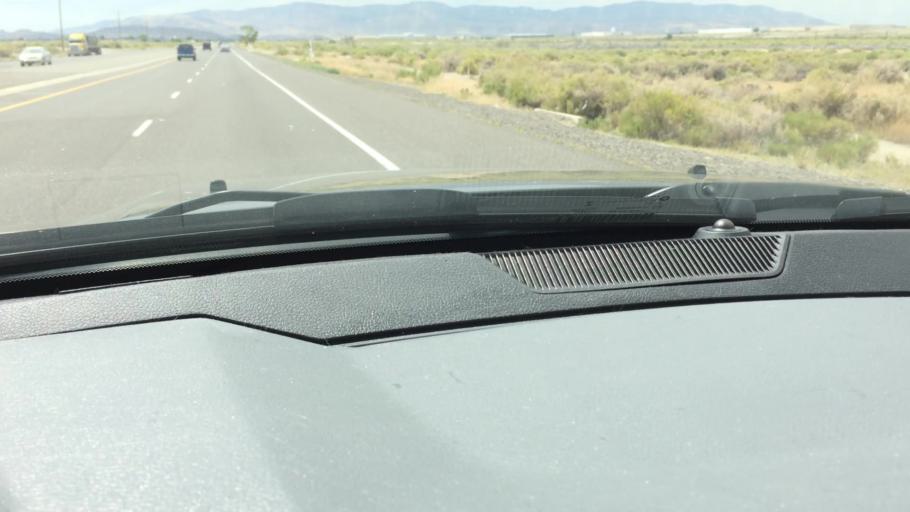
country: US
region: Nevada
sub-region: Lyon County
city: Fernley
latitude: 39.5954
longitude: -119.1744
